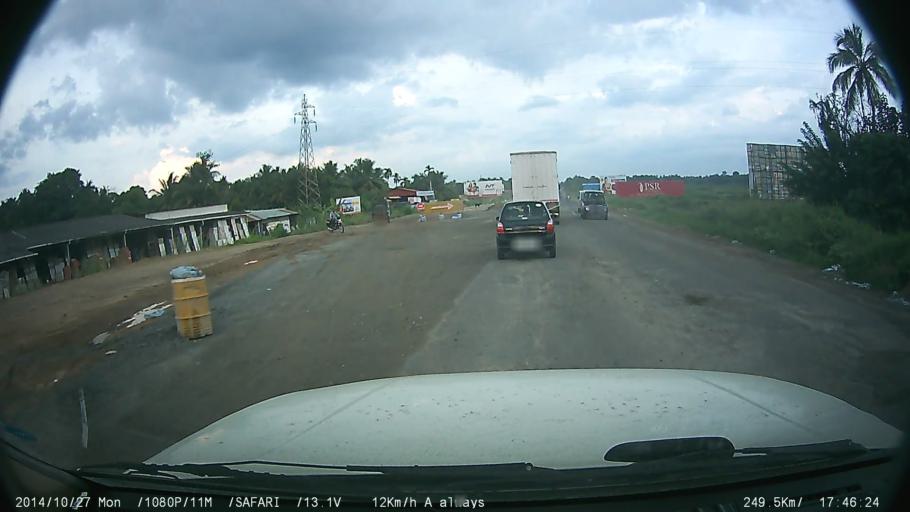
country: IN
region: Kerala
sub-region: Palakkad district
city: Palakkad
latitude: 10.7379
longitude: 76.6201
